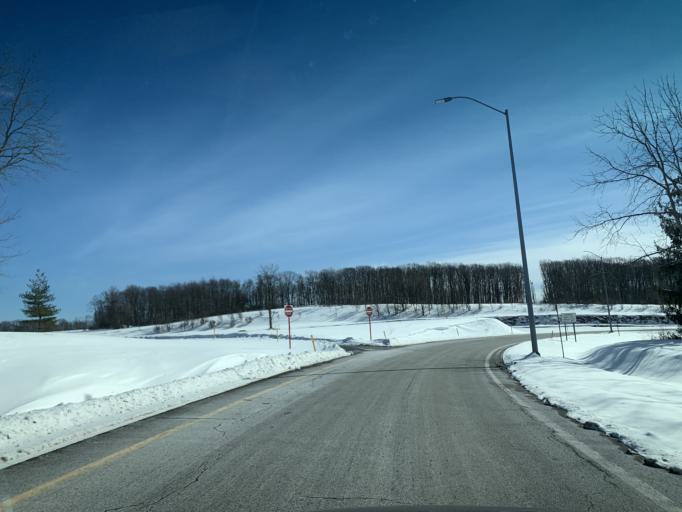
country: US
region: West Virginia
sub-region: Preston County
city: Terra Alta
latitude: 39.6626
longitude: -79.4940
